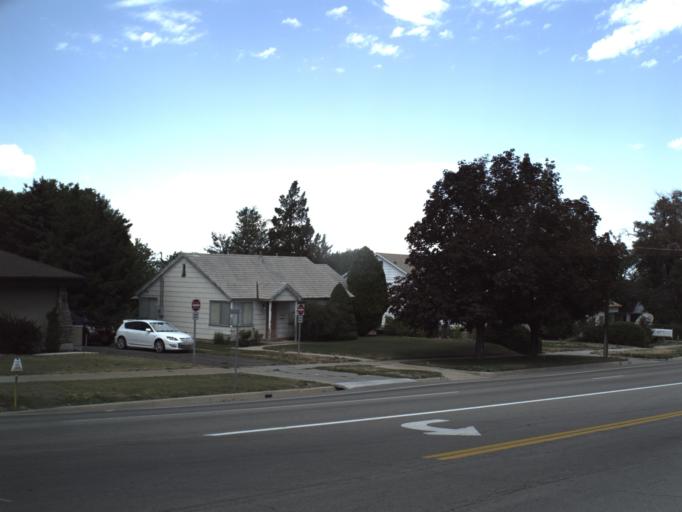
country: US
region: Utah
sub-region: Tooele County
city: Tooele
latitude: 40.5202
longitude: -112.2991
